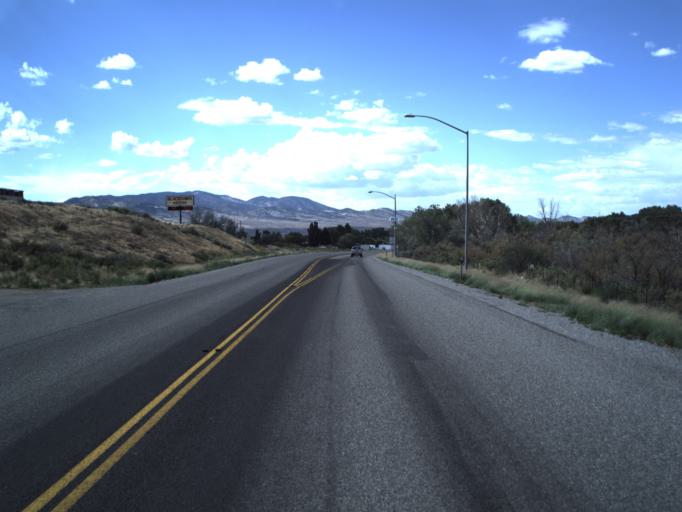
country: US
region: Utah
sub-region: Sevier County
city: Salina
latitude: 38.9468
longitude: -111.8572
